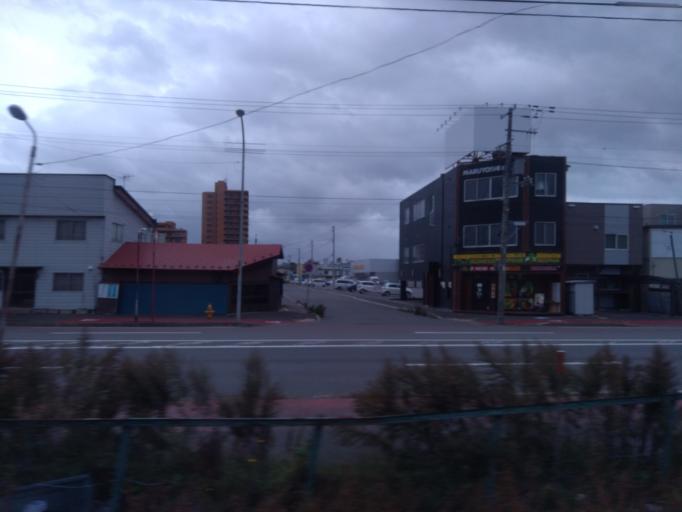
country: JP
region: Hokkaido
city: Hakodate
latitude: 41.7997
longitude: 140.7339
